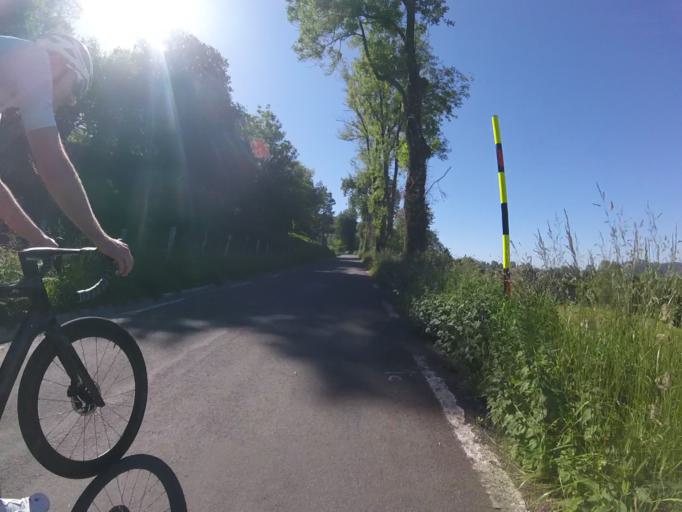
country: ES
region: Basque Country
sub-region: Provincia de Guipuzcoa
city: Beizama
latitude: 43.1239
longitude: -2.1865
